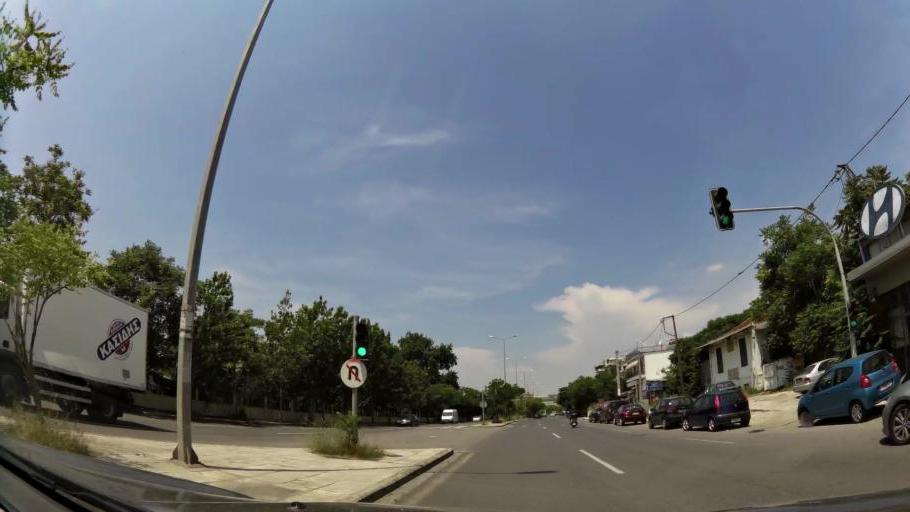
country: GR
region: Central Macedonia
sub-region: Nomos Thessalonikis
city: Thessaloniki
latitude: 40.6425
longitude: 22.9235
